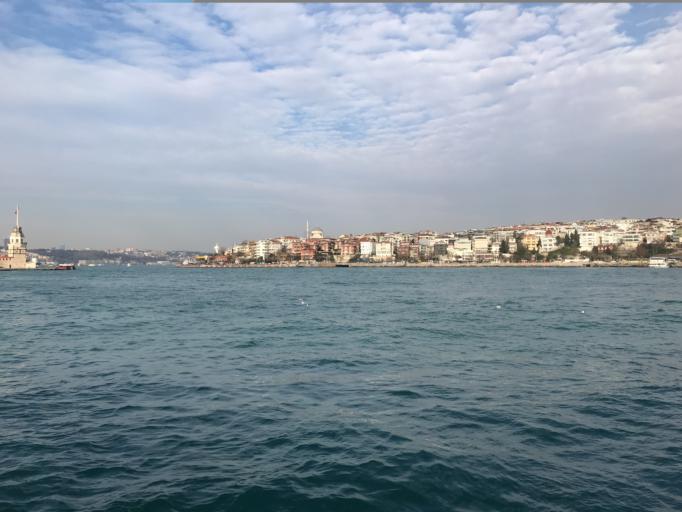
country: TR
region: Istanbul
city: UEskuedar
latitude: 41.0176
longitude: 29.0031
